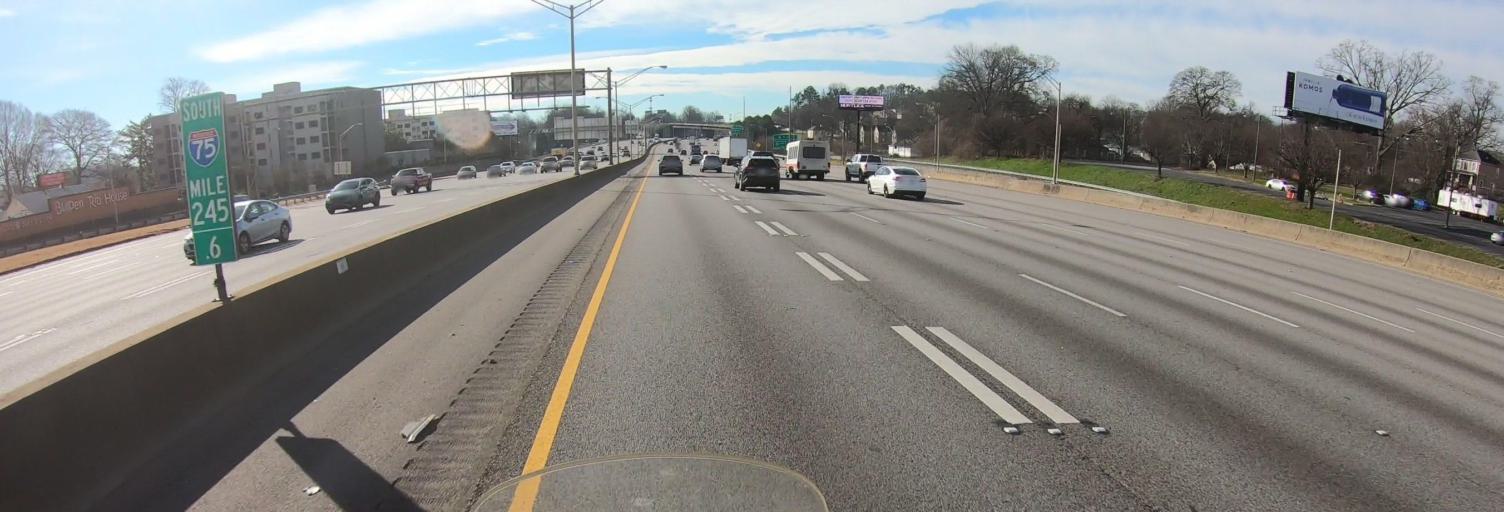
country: US
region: Georgia
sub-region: Fulton County
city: Atlanta
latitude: 33.7325
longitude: -84.3897
